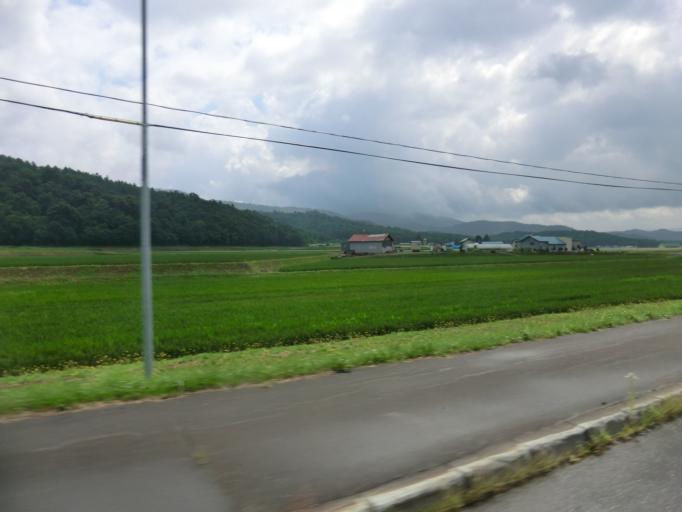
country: JP
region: Hokkaido
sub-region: Asahikawa-shi
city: Asahikawa
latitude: 44.0459
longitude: 142.1475
